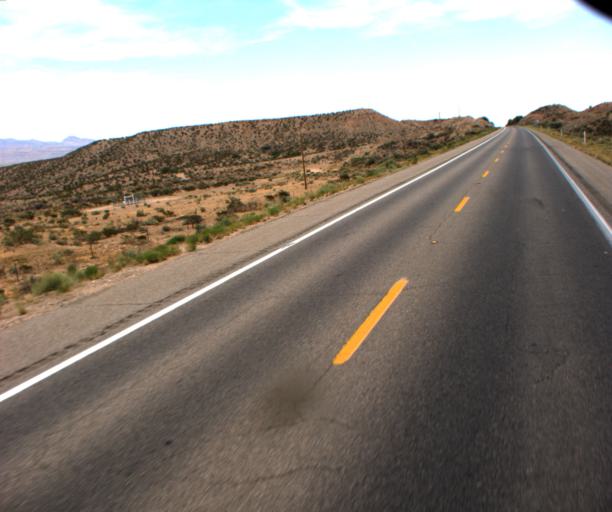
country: US
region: Arizona
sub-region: Graham County
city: Bylas
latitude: 33.0813
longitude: -110.0450
